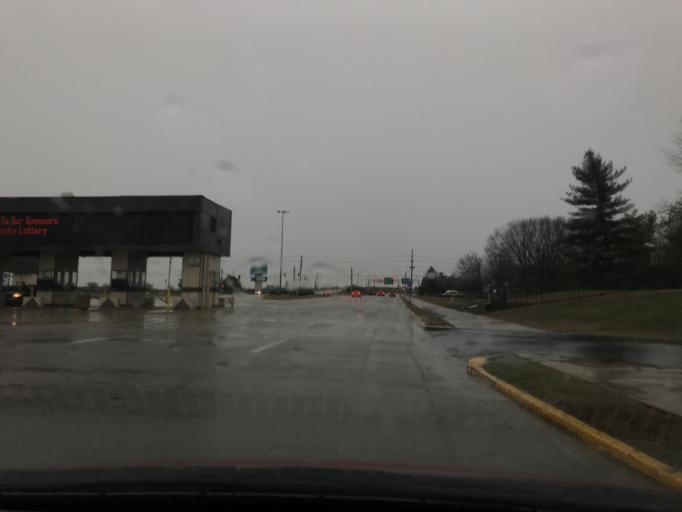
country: US
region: Kentucky
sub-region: Jefferson County
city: Audubon Park
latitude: 38.1953
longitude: -85.7403
